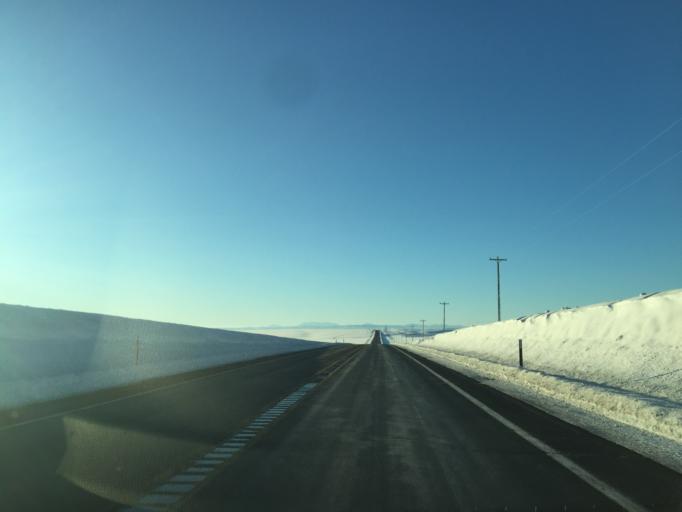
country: US
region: Washington
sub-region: Grant County
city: Soap Lake
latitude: 47.5997
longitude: -119.5375
